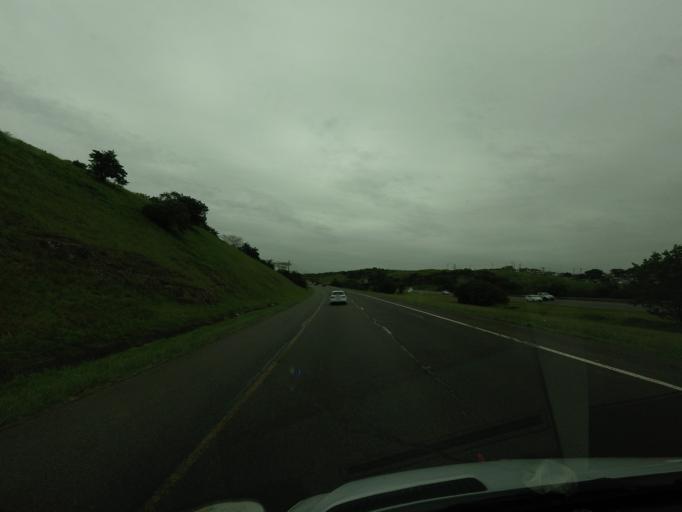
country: ZA
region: KwaZulu-Natal
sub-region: eThekwini Metropolitan Municipality
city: Durban
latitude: -29.6973
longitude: 31.0737
